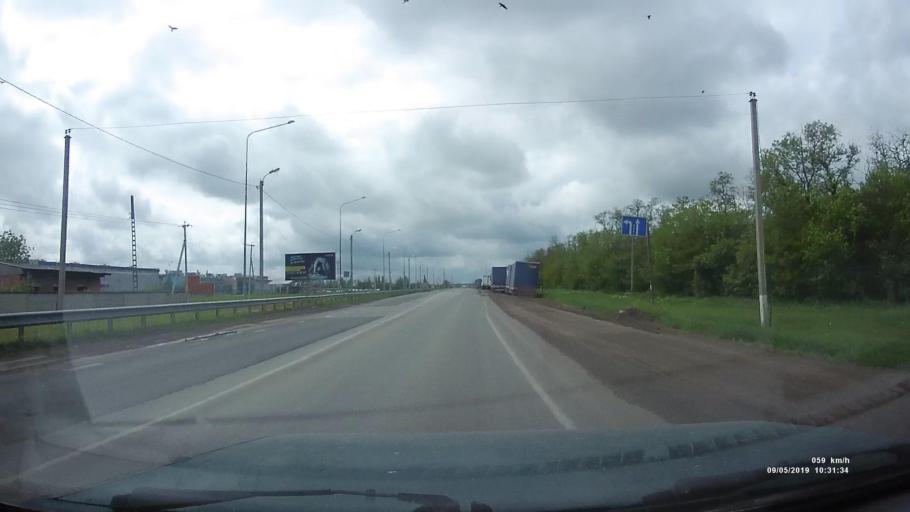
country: RU
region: Rostov
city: Azov
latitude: 47.0804
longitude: 39.4275
